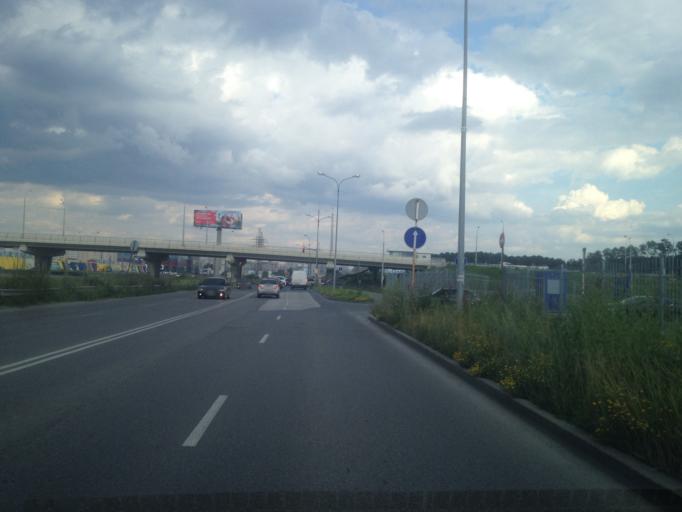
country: RU
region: Sverdlovsk
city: Shirokaya Rechka
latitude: 56.8261
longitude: 60.5111
